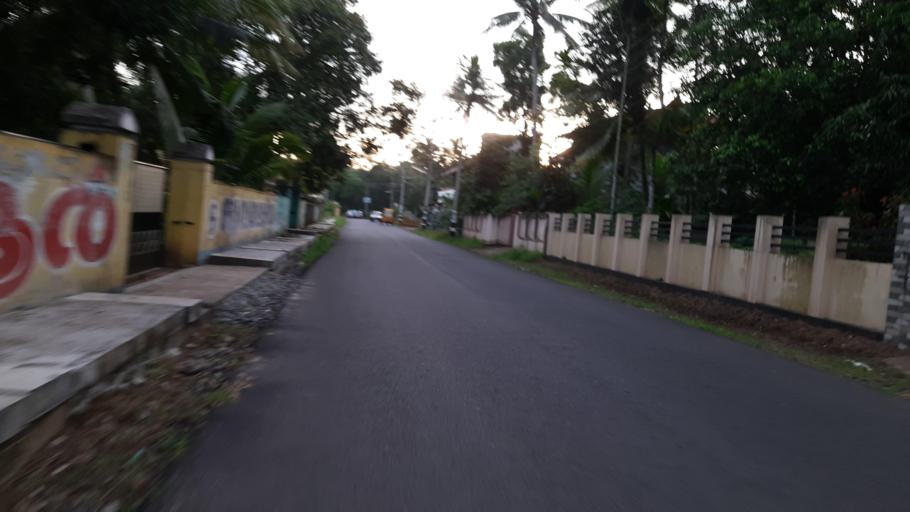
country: IN
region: Kerala
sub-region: Alappuzha
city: Kattanam
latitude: 9.1387
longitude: 76.5494
